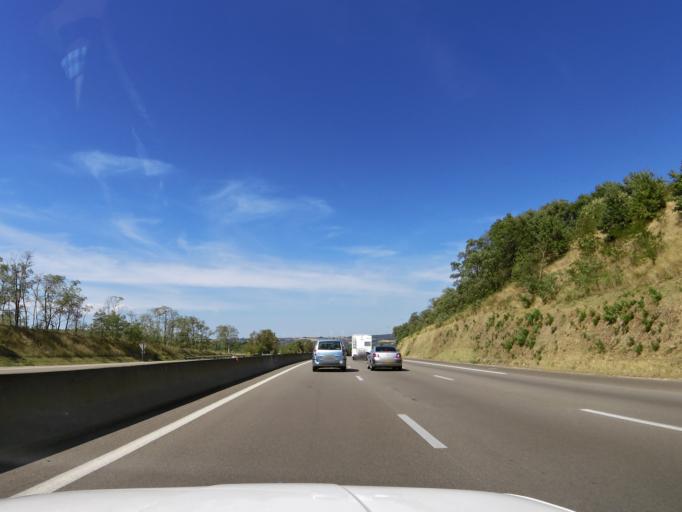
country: FR
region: Rhone-Alpes
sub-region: Departement de la Drome
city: Saint-Barthelemy-de-Vals
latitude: 45.1450
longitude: 4.8890
